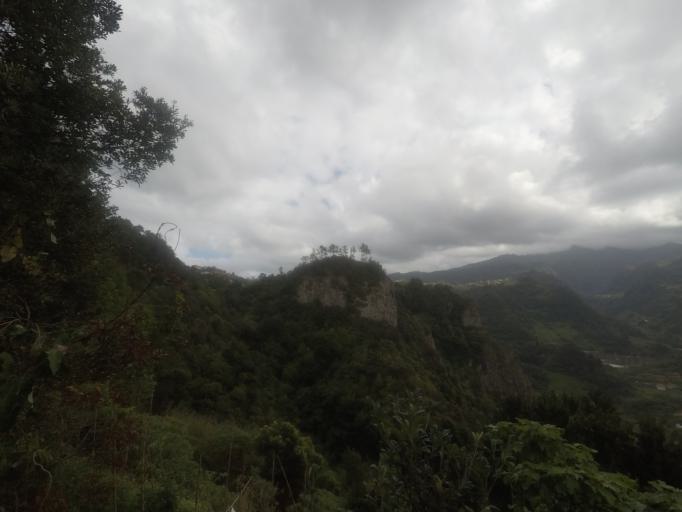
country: PT
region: Madeira
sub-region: Santana
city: Santana
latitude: 32.8272
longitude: -16.8946
